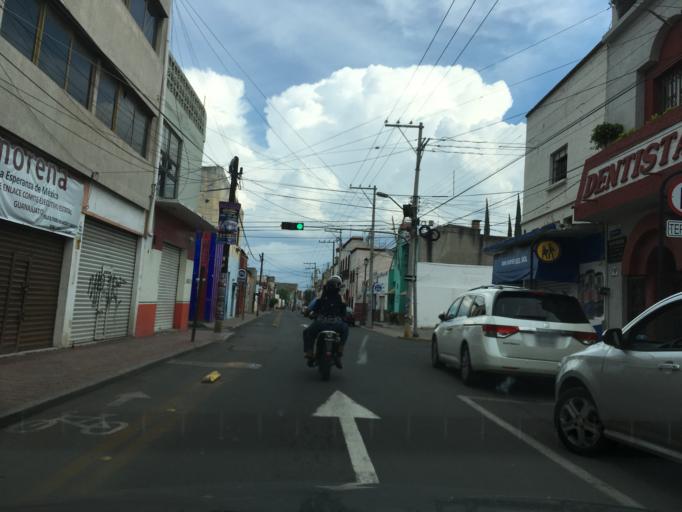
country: MX
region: Guanajuato
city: Celaya
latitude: 20.5265
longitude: -100.8179
